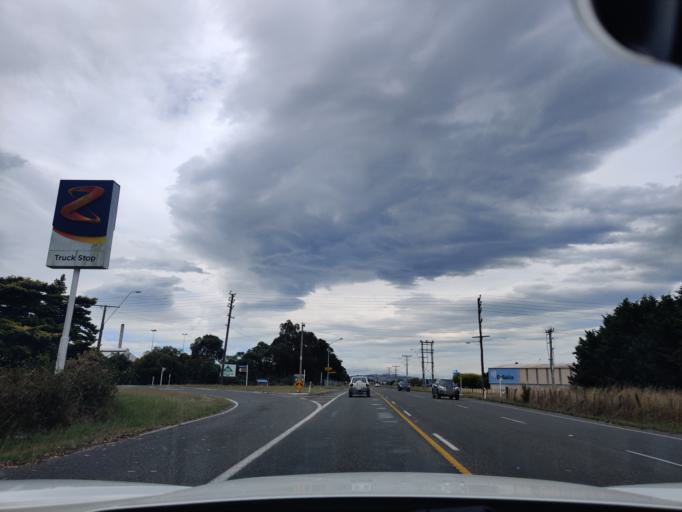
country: NZ
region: Wellington
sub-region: Masterton District
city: Masterton
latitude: -40.9703
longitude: 175.6013
